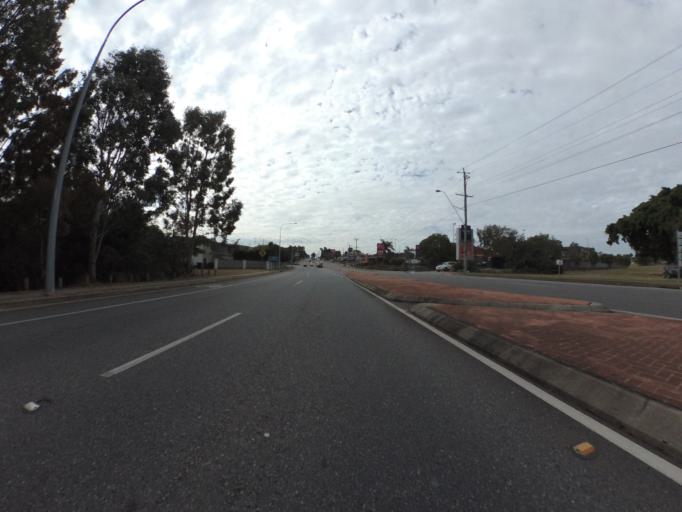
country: AU
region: Queensland
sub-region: Brisbane
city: Wynnum West
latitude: -27.4584
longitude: 153.1522
